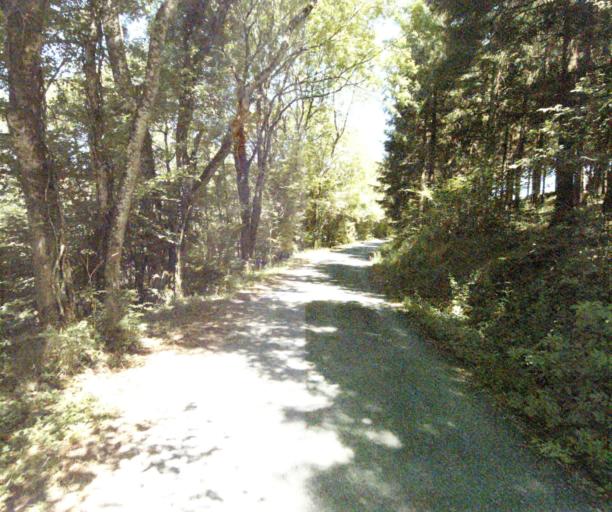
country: FR
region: Midi-Pyrenees
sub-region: Departement du Tarn
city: Dourgne
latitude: 43.4232
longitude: 2.1724
